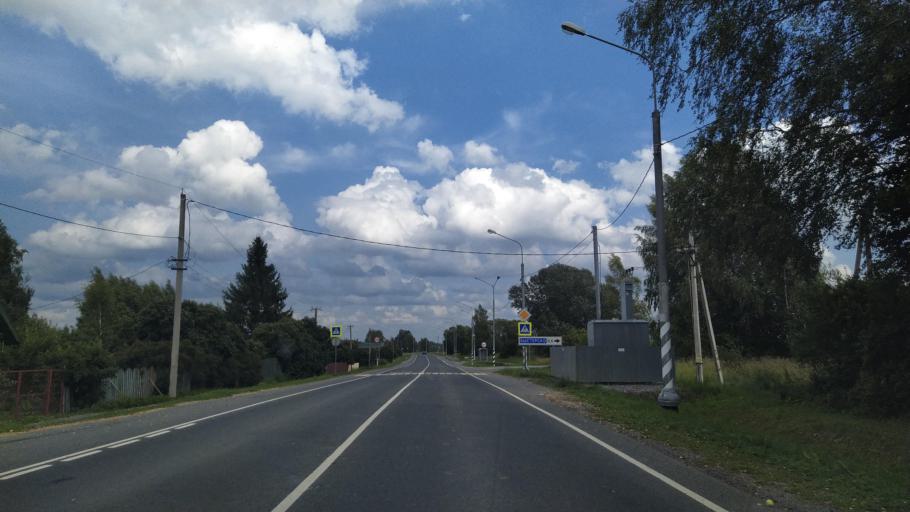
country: RU
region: Pskov
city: Dno
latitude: 58.0613
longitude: 30.0142
